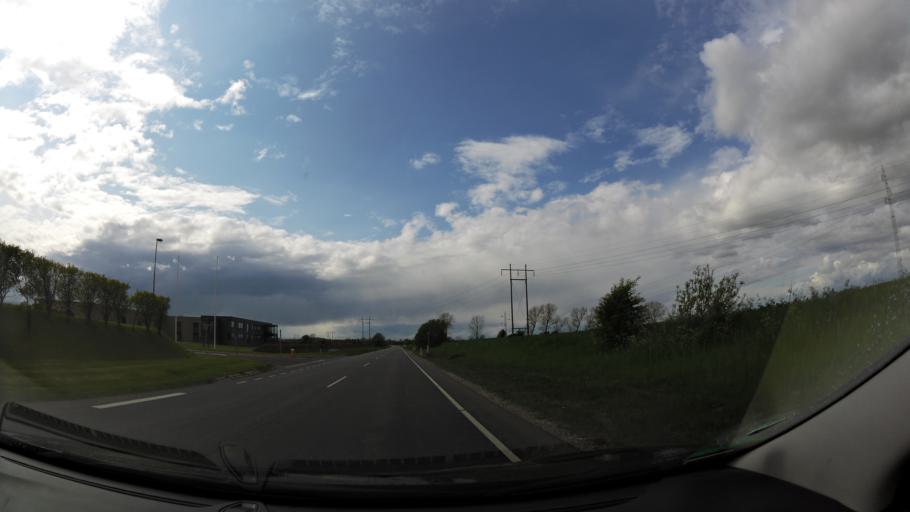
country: DK
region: South Denmark
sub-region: Nyborg Kommune
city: Nyborg
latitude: 55.3172
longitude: 10.7502
